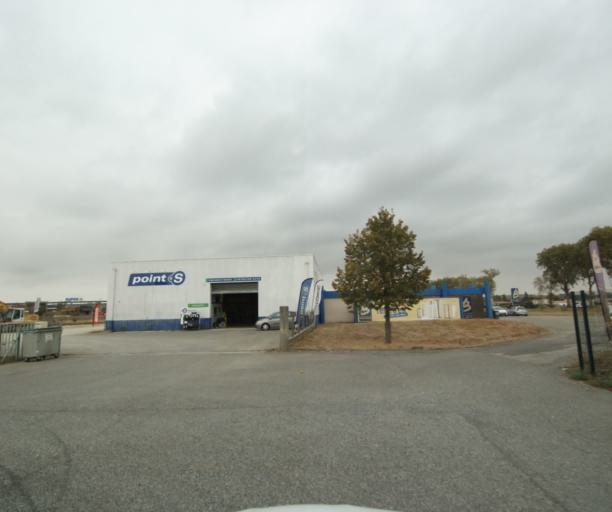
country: FR
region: Midi-Pyrenees
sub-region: Departement de la Haute-Garonne
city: Villefranche-de-Lauragais
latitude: 43.3970
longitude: 1.7029
